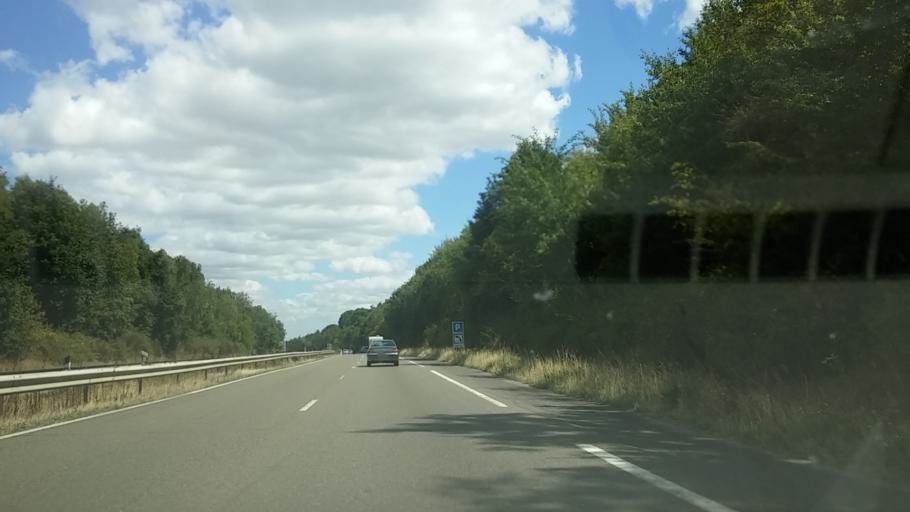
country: FR
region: Ile-de-France
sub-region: Departement des Yvelines
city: La Queue-les-Yvelines
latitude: 48.7984
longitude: 1.7536
